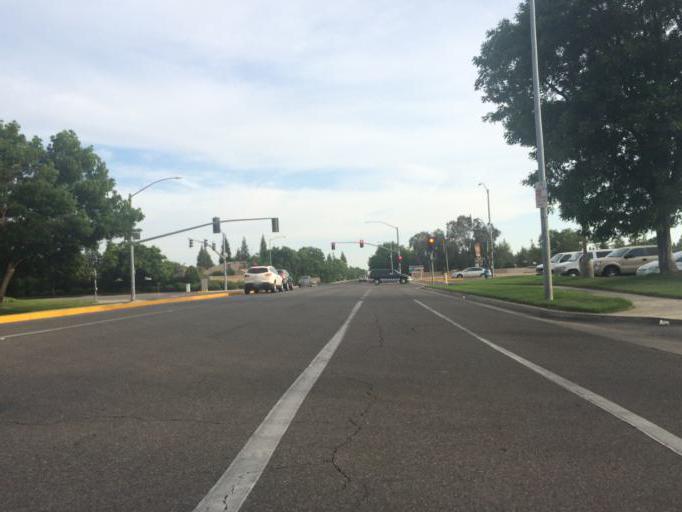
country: US
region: California
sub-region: Fresno County
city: Tarpey Village
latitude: 36.8093
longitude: -119.6730
